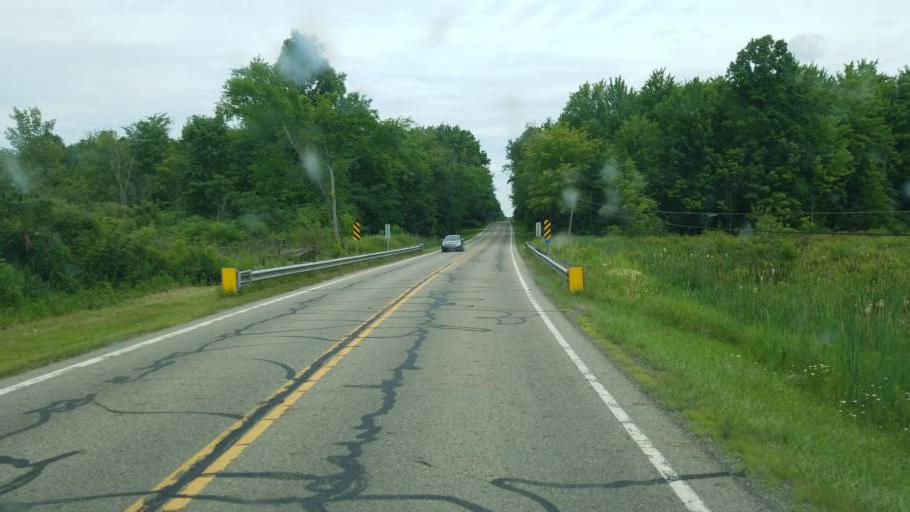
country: US
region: Ohio
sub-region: Geauga County
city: Bainbridge
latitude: 41.4249
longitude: -81.2479
